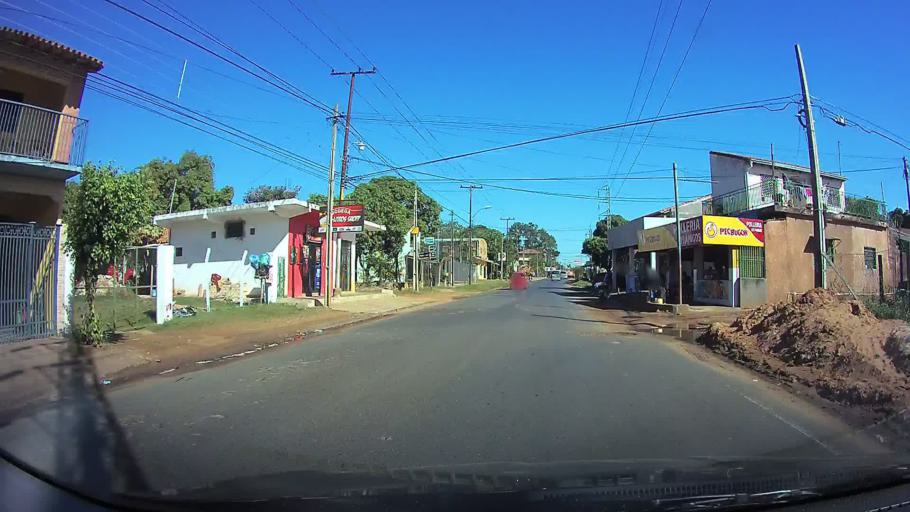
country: PY
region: Central
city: Fernando de la Mora
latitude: -25.3565
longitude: -57.5452
